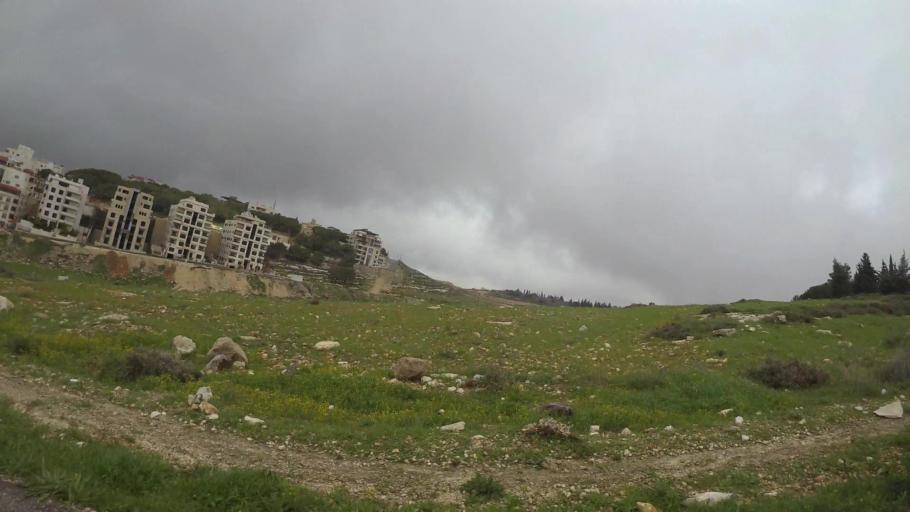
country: JO
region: Amman
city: Umm as Summaq
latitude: 31.9160
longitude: 35.8652
